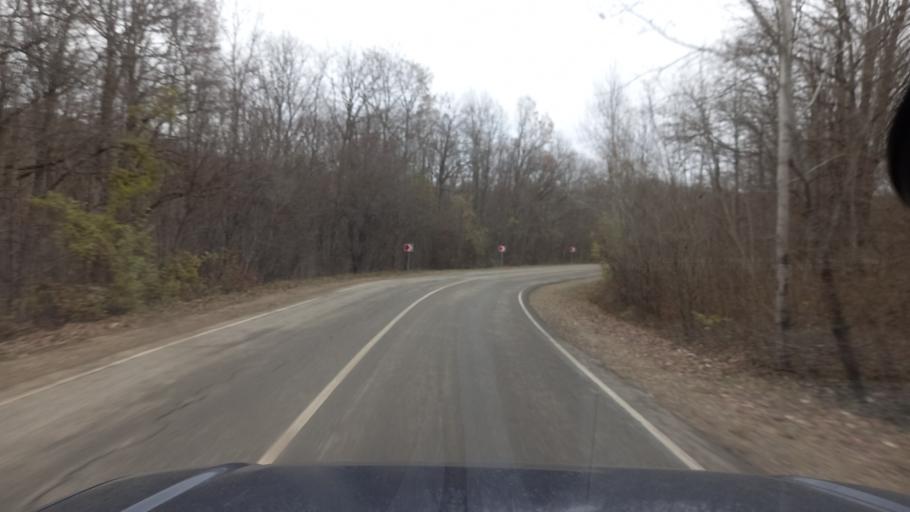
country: RU
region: Krasnodarskiy
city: Goryachiy Klyuch
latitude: 44.5439
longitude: 39.2649
